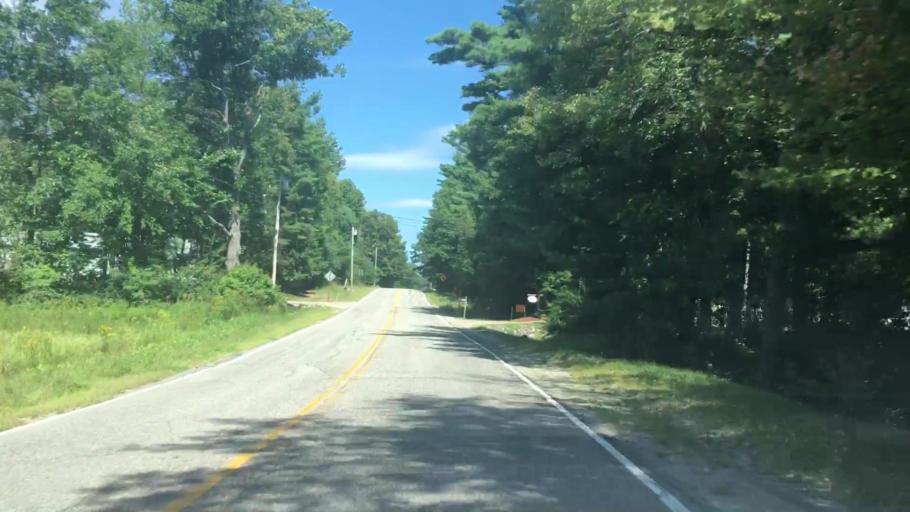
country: US
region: Maine
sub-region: Kennebec County
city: Monmouth
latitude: 44.1521
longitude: -69.9480
